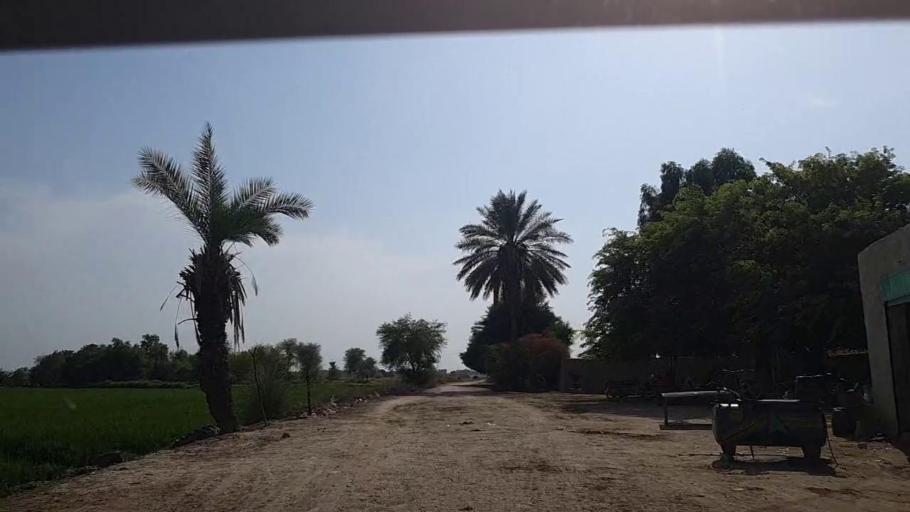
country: PK
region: Sindh
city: Khanpur
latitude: 27.8473
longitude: 69.3463
